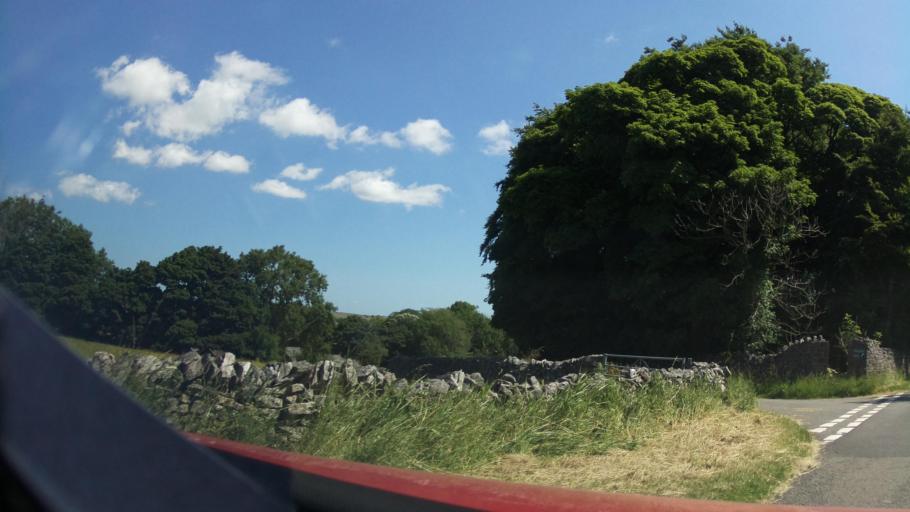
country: GB
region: England
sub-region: Derbyshire
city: Tideswell
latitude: 53.2741
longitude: -1.8296
